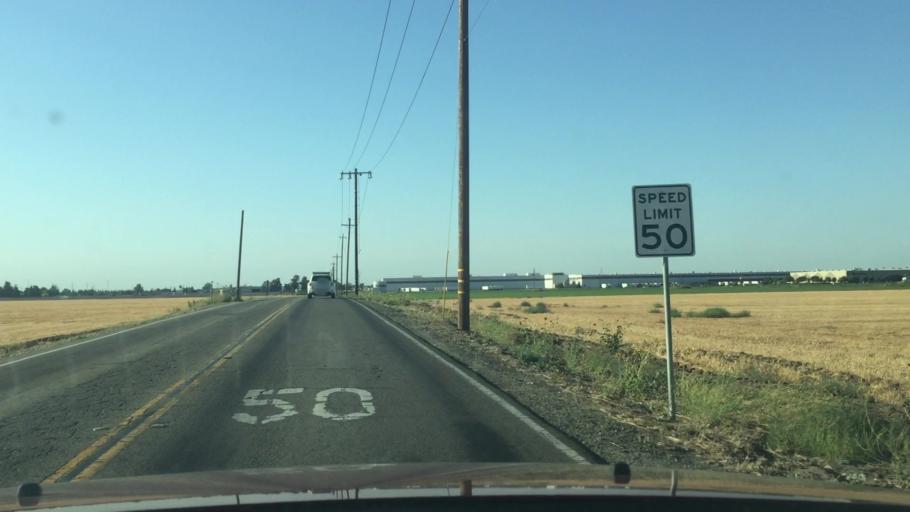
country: US
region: California
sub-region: San Joaquin County
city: Lathrop
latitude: 37.7979
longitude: -121.2706
